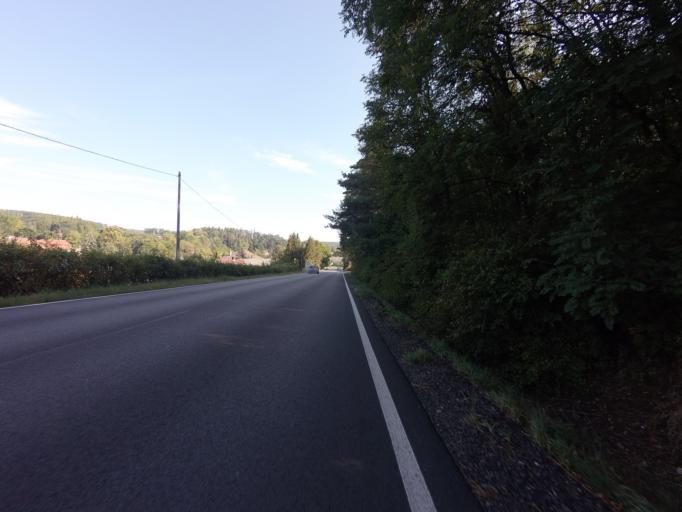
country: CZ
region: Jihocesky
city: Tyn nad Vltavou
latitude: 49.2508
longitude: 14.4213
